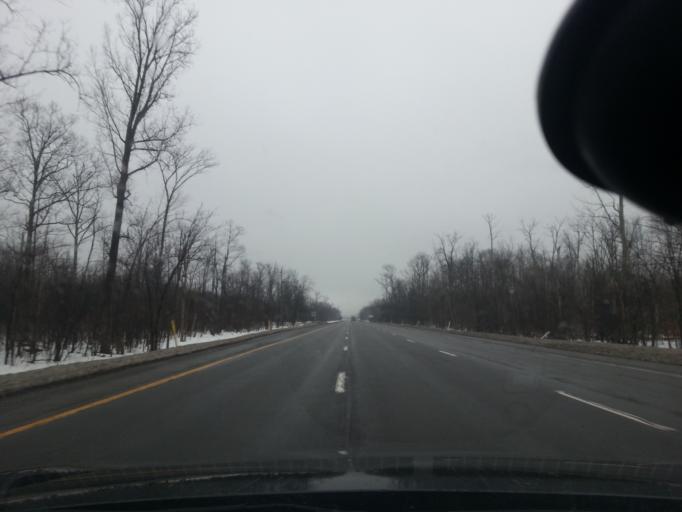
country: US
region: New York
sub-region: Jefferson County
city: Adams
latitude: 43.7214
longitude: -76.0771
